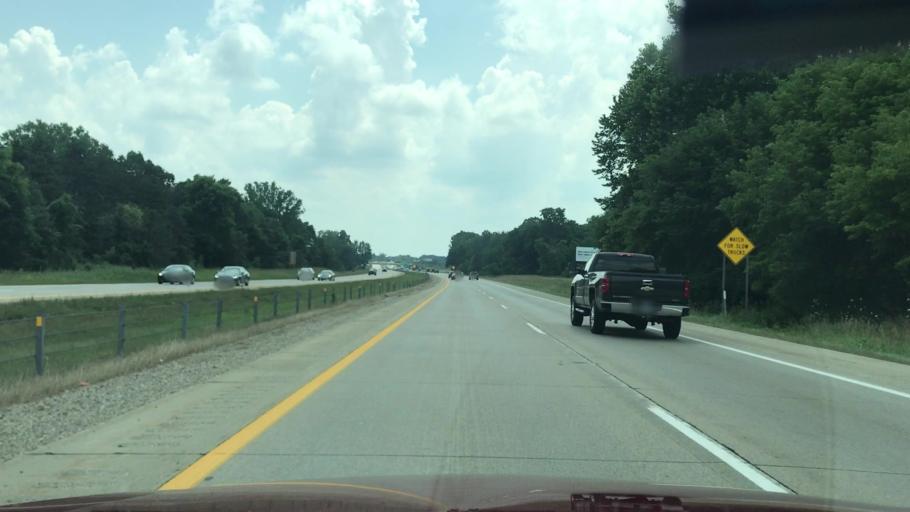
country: US
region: Michigan
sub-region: Allegan County
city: Plainwell
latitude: 42.4744
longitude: -85.6531
